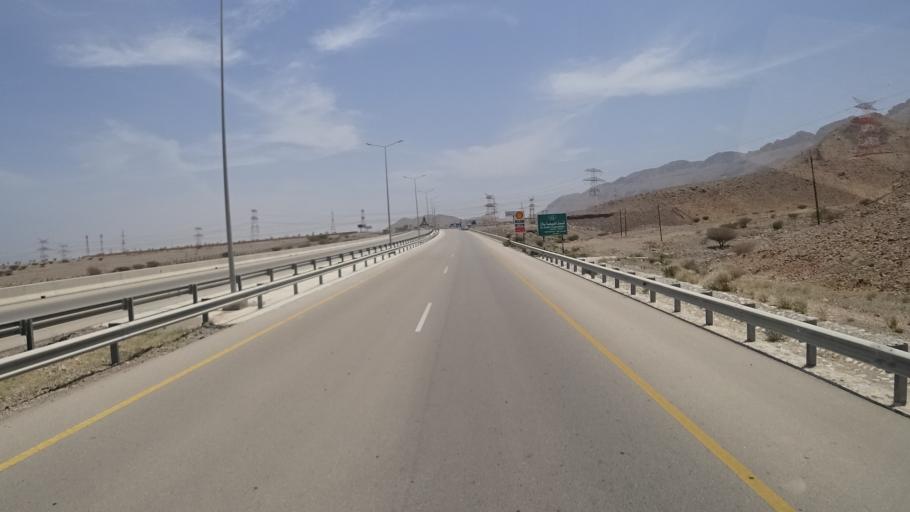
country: OM
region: Ash Sharqiyah
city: Sur
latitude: 22.6551
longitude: 59.3926
